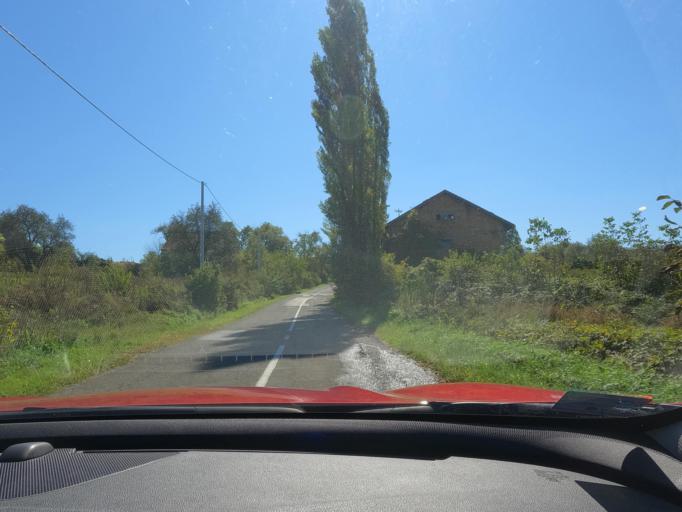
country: HR
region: Sisacko-Moslavacka
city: Petrinja
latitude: 45.3416
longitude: 16.2502
